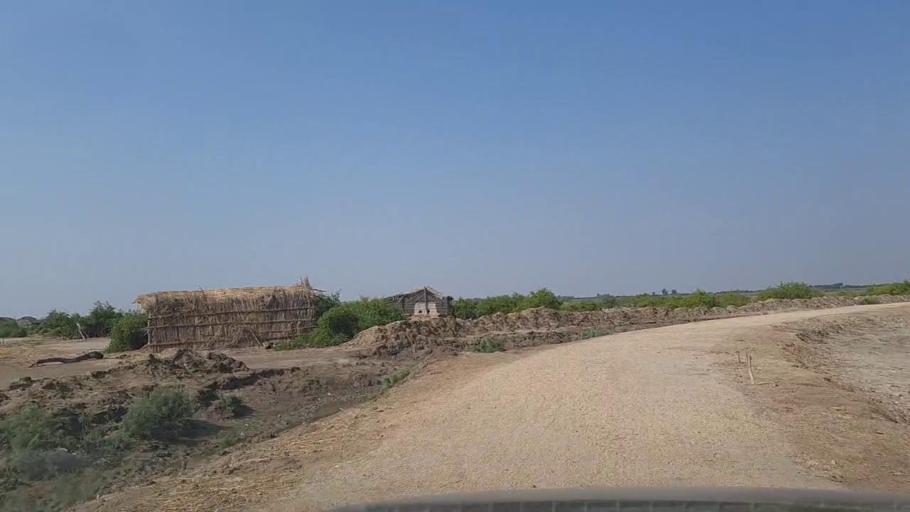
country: PK
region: Sindh
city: Mirpur Sakro
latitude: 24.5070
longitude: 67.7804
